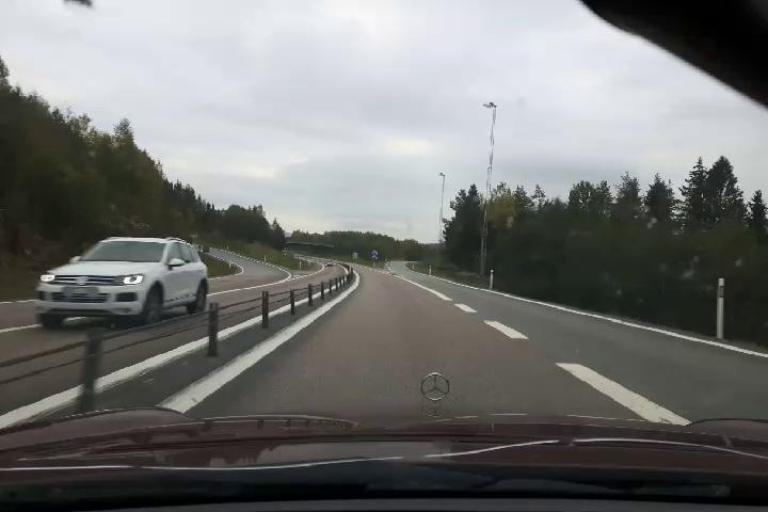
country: SE
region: Vaesternorrland
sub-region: Kramfors Kommun
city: Nordingra
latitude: 62.9327
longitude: 18.0953
